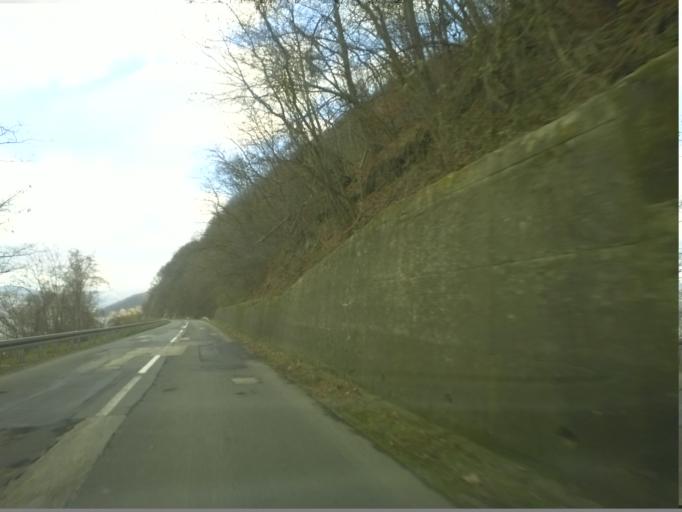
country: RO
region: Caras-Severin
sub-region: Comuna Berzasca
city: Liubcova
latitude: 44.6435
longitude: 21.8827
